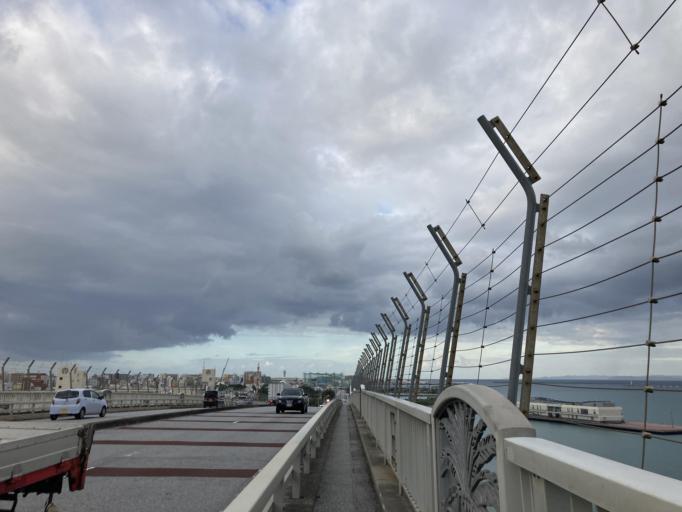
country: JP
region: Okinawa
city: Naha-shi
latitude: 26.2266
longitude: 127.6800
